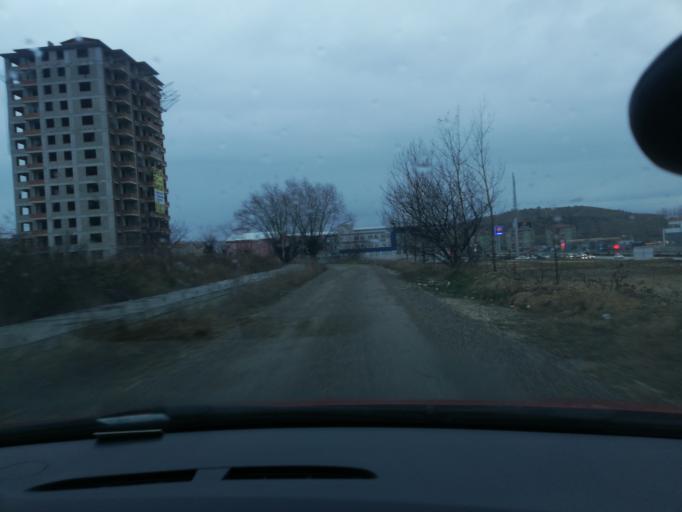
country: TR
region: Kastamonu
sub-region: Cide
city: Kastamonu
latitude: 41.4200
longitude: 33.8011
